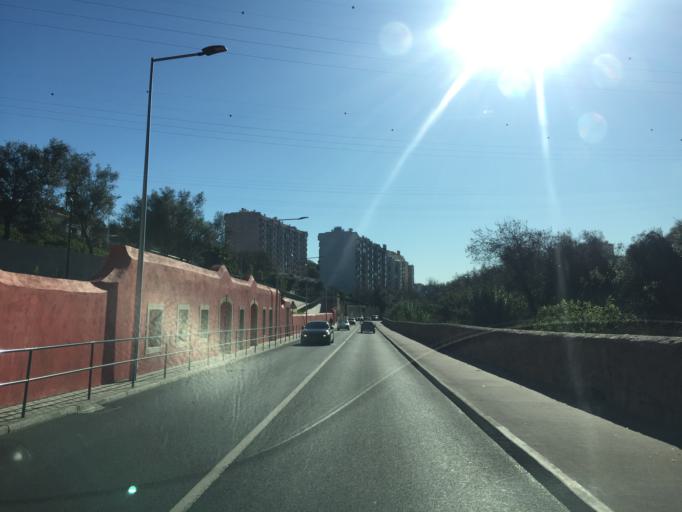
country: PT
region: Lisbon
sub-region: Sintra
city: Belas
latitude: 38.7718
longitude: -9.2612
